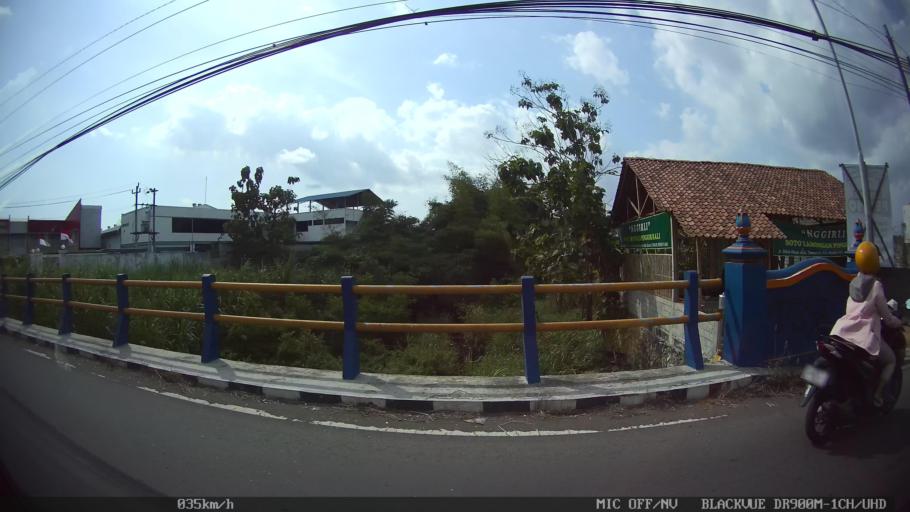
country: ID
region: Daerah Istimewa Yogyakarta
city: Kasihan
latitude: -7.8283
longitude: 110.3229
